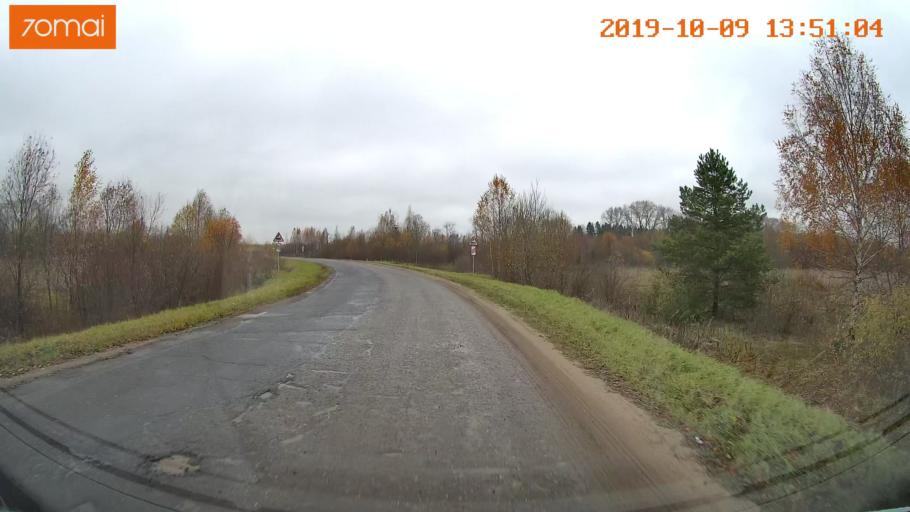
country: RU
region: Kostroma
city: Buy
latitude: 58.4058
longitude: 41.2418
